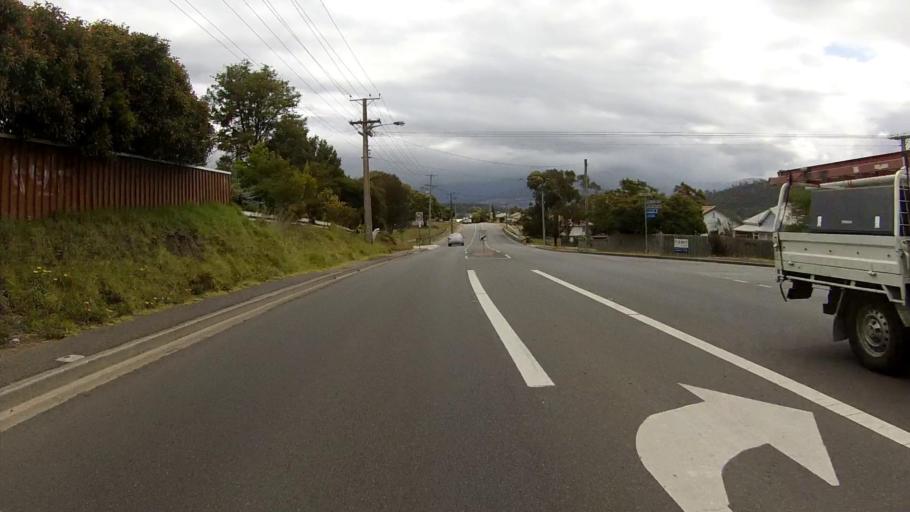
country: AU
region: Tasmania
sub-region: Clarence
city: Warrane
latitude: -42.8596
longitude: 147.3831
